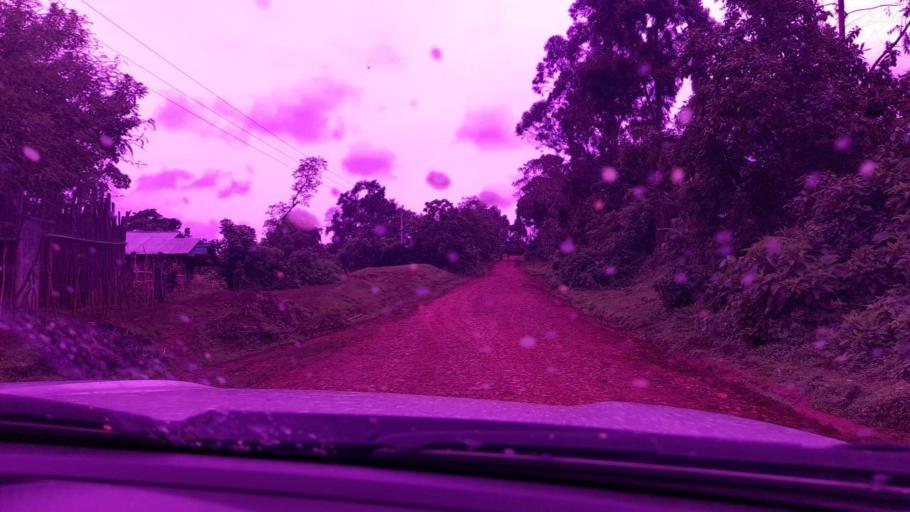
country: ET
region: Southern Nations, Nationalities, and People's Region
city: Tippi
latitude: 7.5682
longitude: 35.6534
